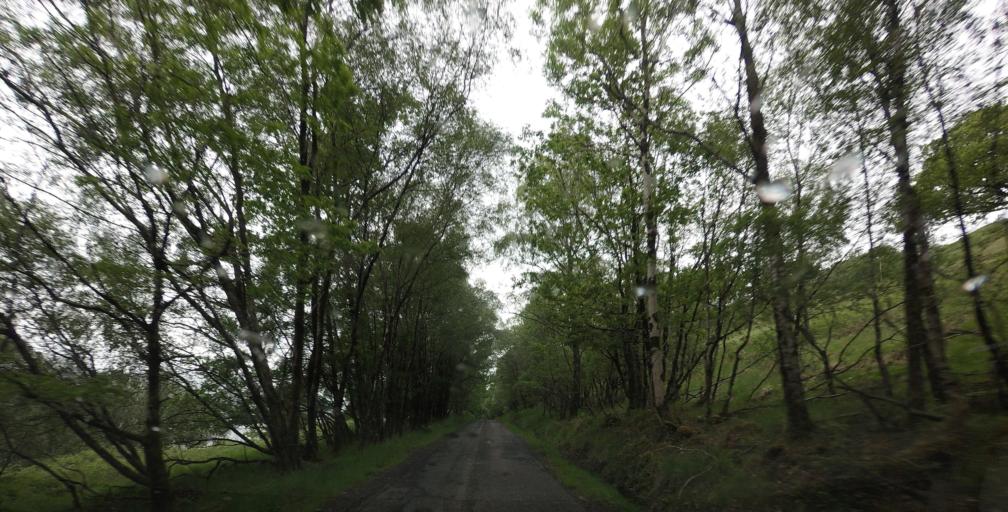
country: GB
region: Scotland
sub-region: Highland
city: Fort William
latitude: 56.8093
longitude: -5.1477
